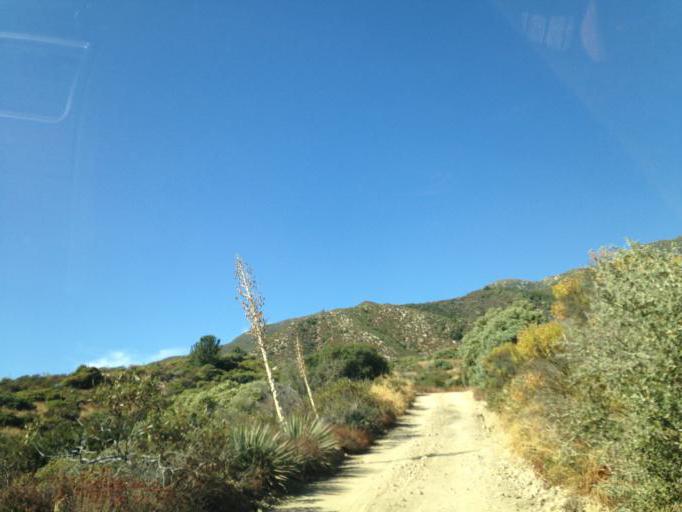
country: US
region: California
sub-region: San Bernardino County
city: Running Springs
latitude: 34.1638
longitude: -117.0778
